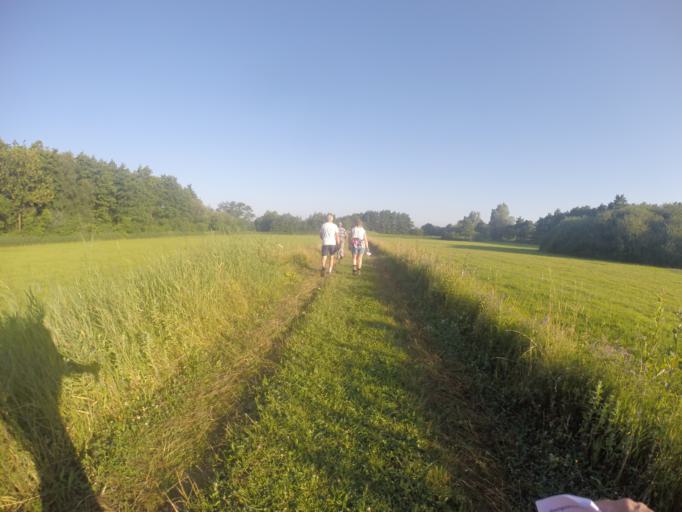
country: NL
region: Gelderland
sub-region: Gemeente Lochem
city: Barchem
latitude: 52.1176
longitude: 6.4281
